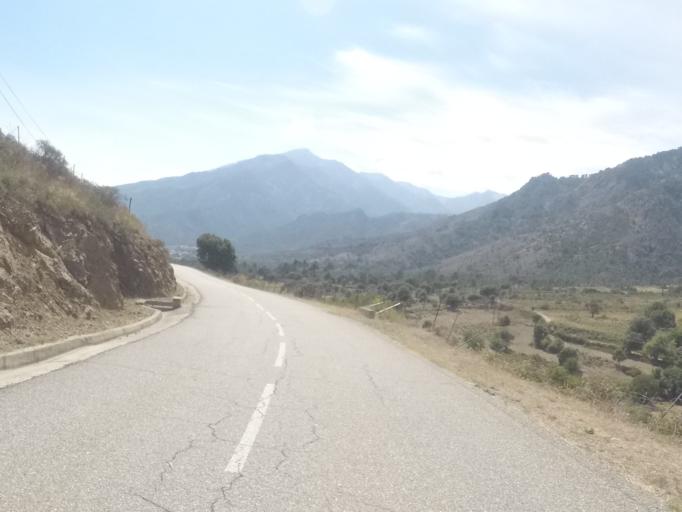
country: FR
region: Corsica
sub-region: Departement de la Haute-Corse
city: Corte
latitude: 42.3397
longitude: 9.1497
